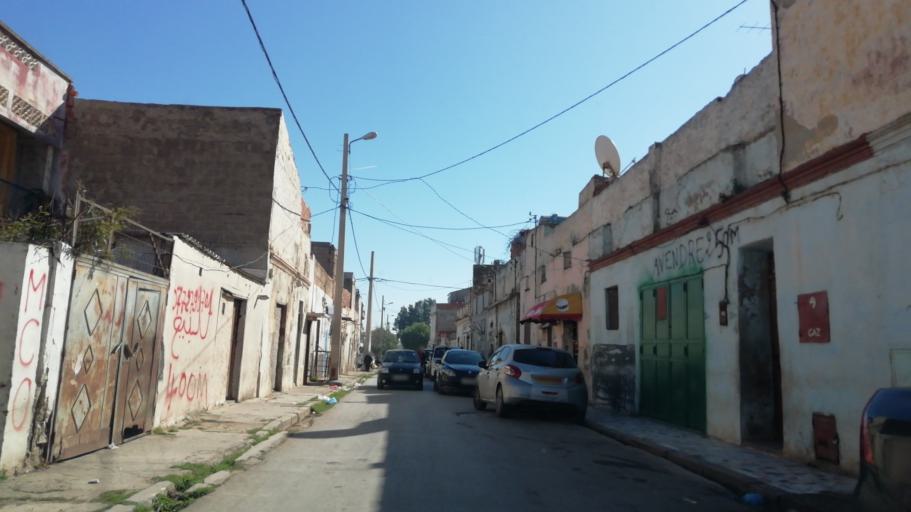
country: DZ
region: Oran
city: Oran
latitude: 35.6881
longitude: -0.6374
